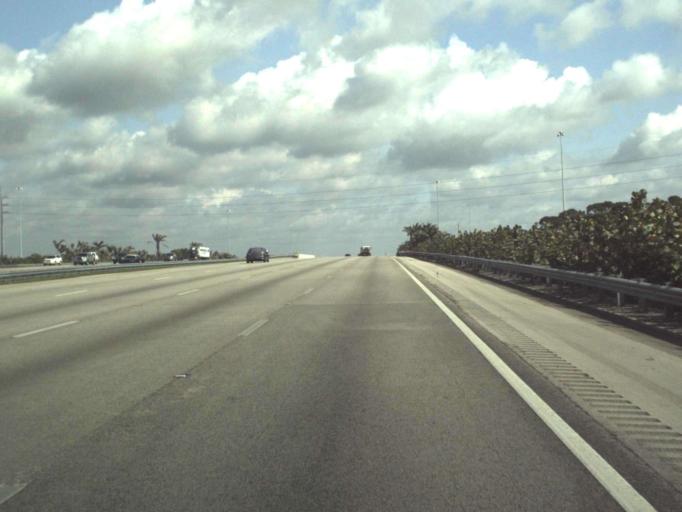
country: US
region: Florida
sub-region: Palm Beach County
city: Palm Beach Gardens
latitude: 26.8810
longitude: -80.1269
